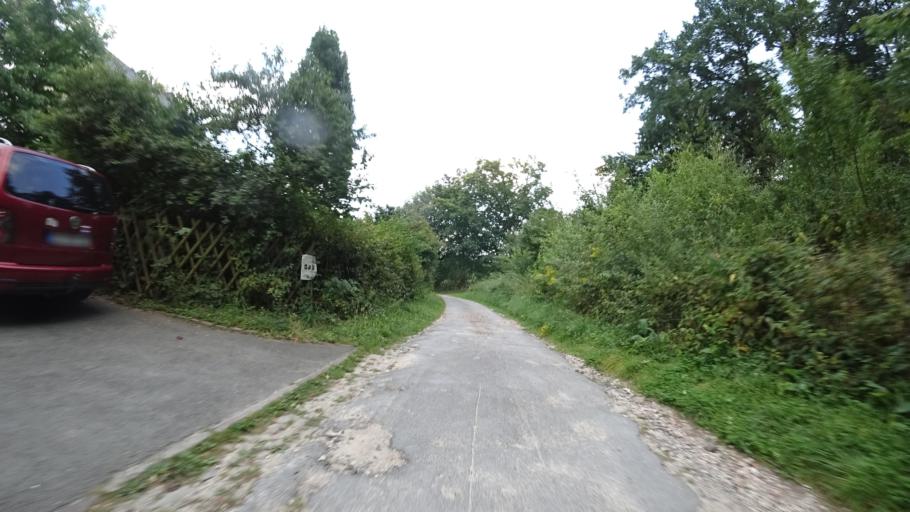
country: DE
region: North Rhine-Westphalia
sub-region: Regierungsbezirk Detmold
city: Bielefeld
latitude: 52.0101
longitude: 8.4990
